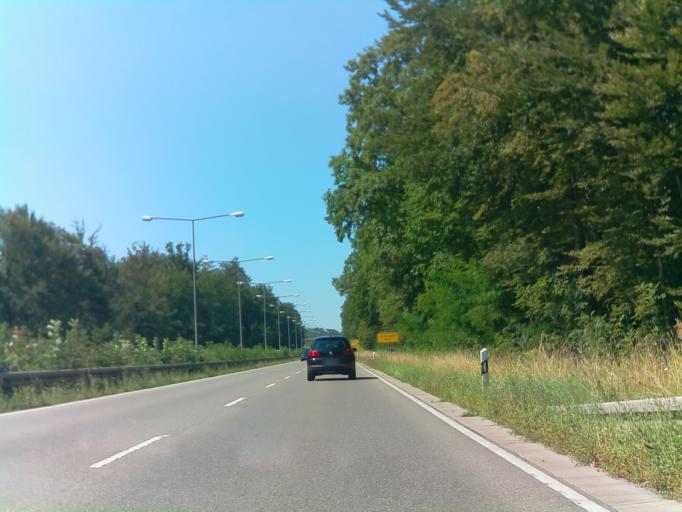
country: DE
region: Baden-Wuerttemberg
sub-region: Regierungsbezirk Stuttgart
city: Gerlingen
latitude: 48.7721
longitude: 9.1025
